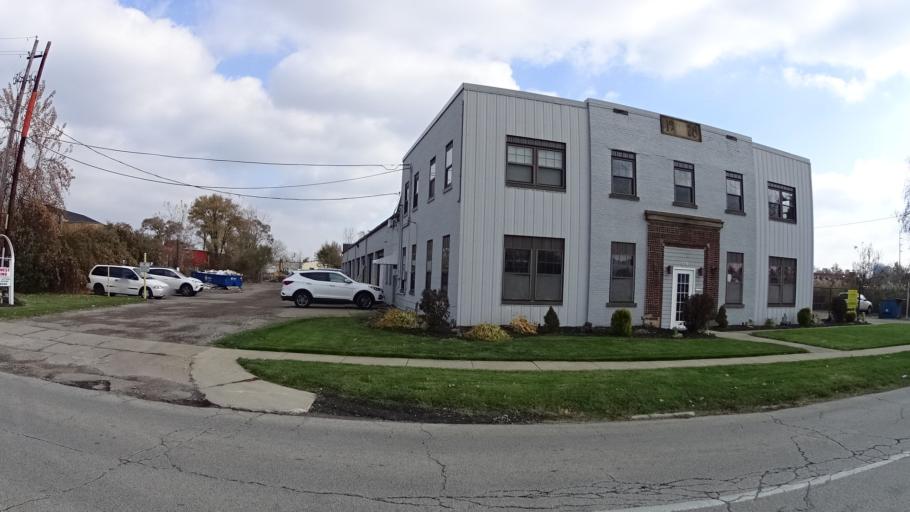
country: US
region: Ohio
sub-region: Lorain County
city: Elyria
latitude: 41.3731
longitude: -82.0859
